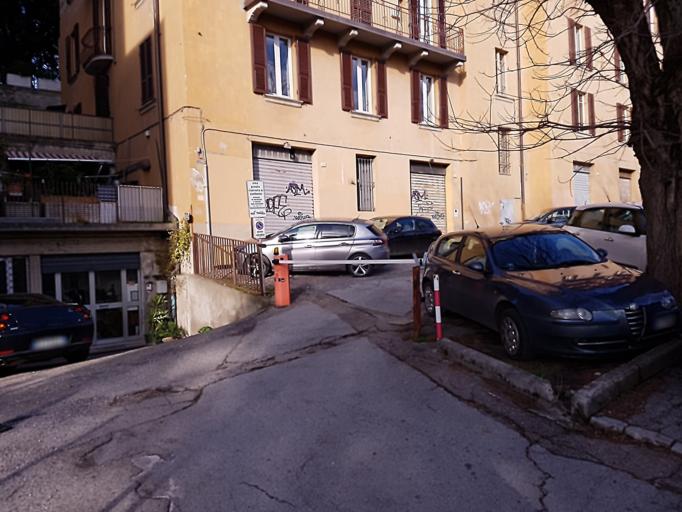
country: IT
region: Umbria
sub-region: Provincia di Perugia
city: Perugia
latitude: 43.1045
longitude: 12.3887
